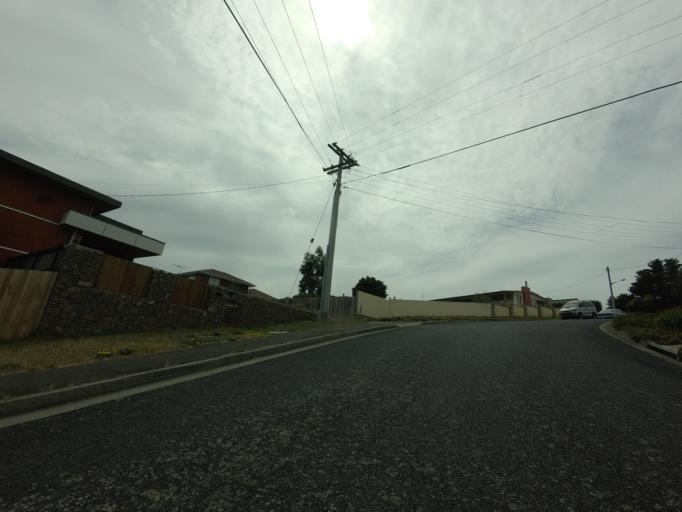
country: AU
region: Tasmania
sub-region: Sorell
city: Sorell
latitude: -42.7961
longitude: 147.5274
